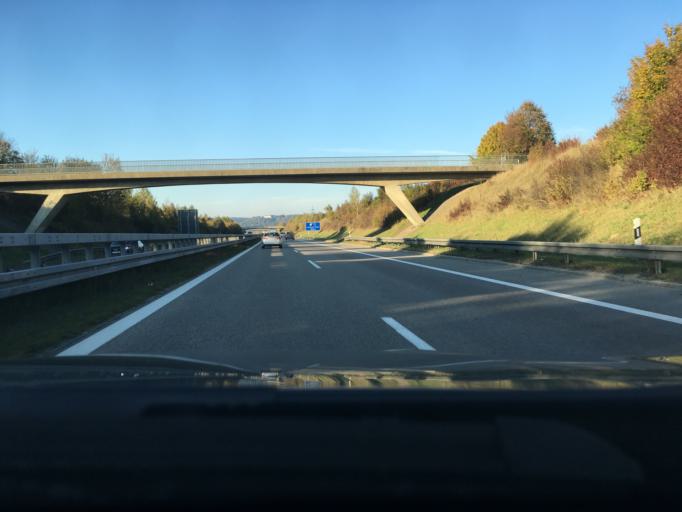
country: DE
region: Baden-Wuerttemberg
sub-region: Tuebingen Region
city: Leutkirch im Allgau
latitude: 47.8206
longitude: 9.9915
